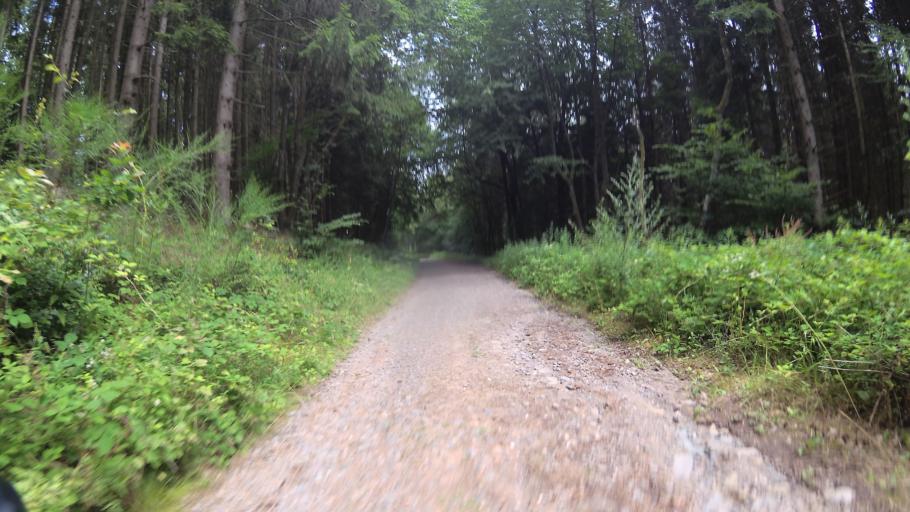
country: DE
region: Saarland
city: Marpingen
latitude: 49.4606
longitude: 7.0988
